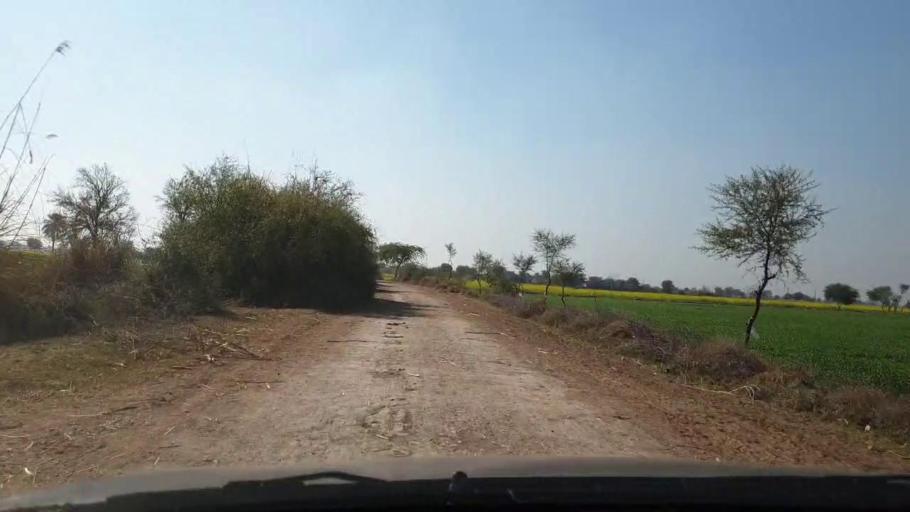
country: PK
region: Sindh
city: Jhol
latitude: 25.9255
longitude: 68.7956
